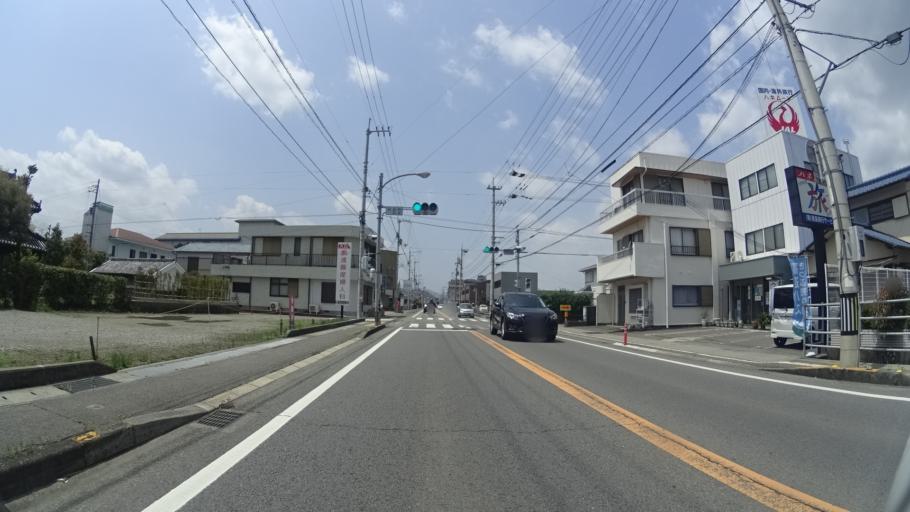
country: JP
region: Tokushima
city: Ishii
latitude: 34.0687
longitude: 134.4477
